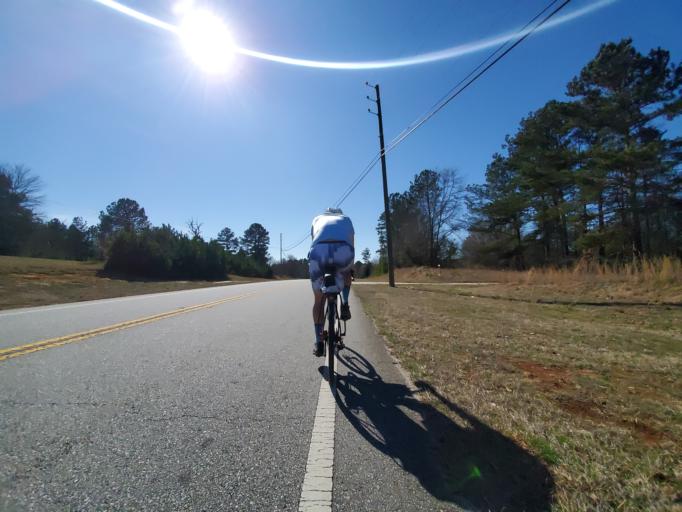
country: US
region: Georgia
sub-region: Gwinnett County
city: Dacula
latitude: 33.9652
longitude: -83.9100
